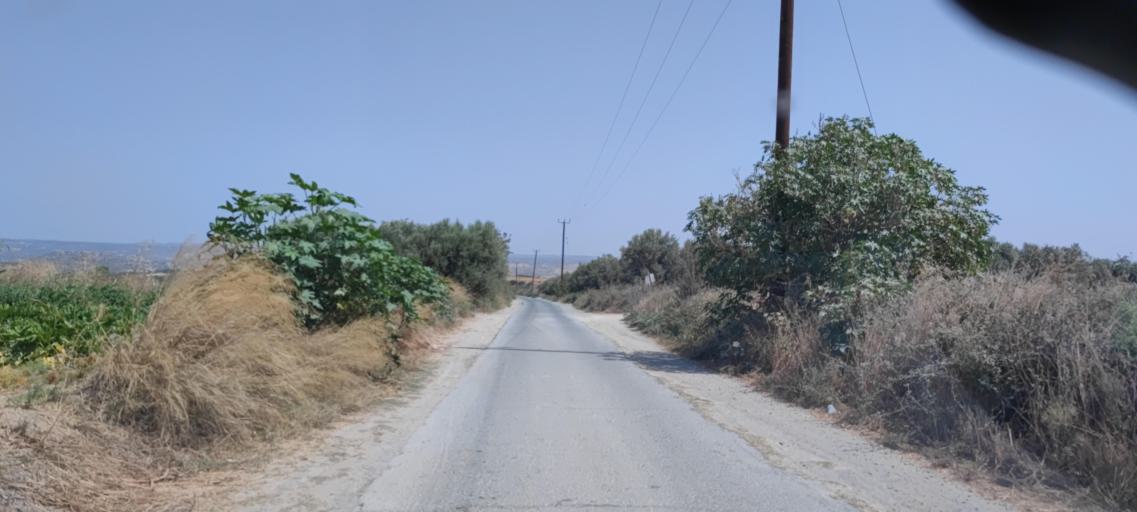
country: CY
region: Limassol
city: Pissouri
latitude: 34.6615
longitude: 32.7674
